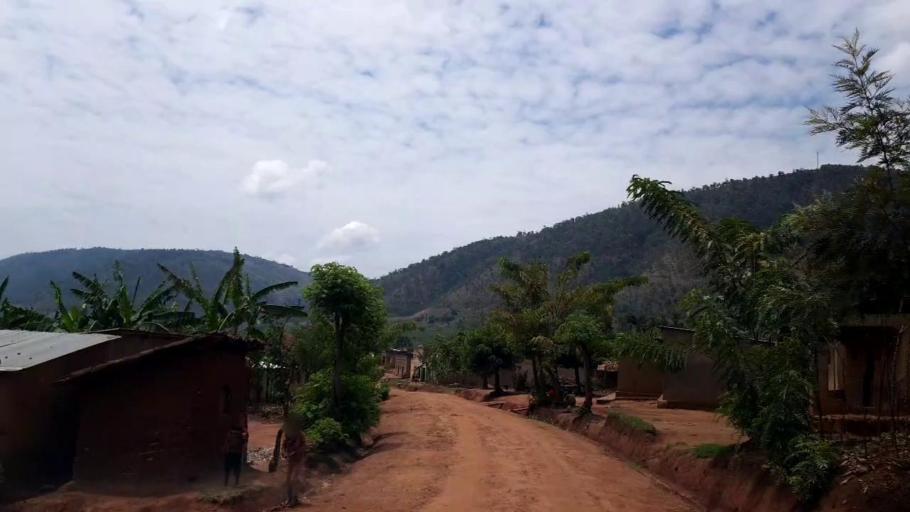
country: RW
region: Northern Province
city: Byumba
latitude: -1.4963
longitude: 30.1946
